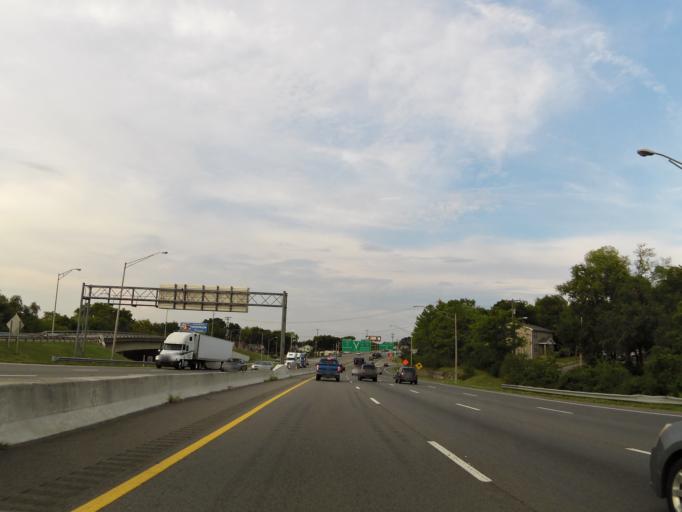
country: US
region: Tennessee
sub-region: Davidson County
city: Nashville
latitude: 36.1658
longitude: -86.8179
